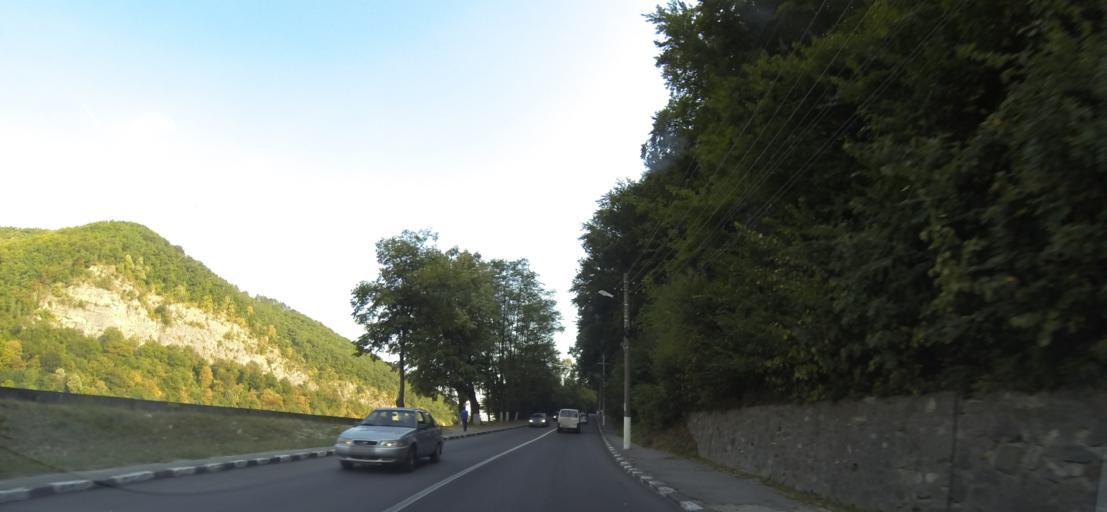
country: RO
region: Valcea
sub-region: Oras Calimanesti
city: Jiblea Veche
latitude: 45.2559
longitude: 24.3341
